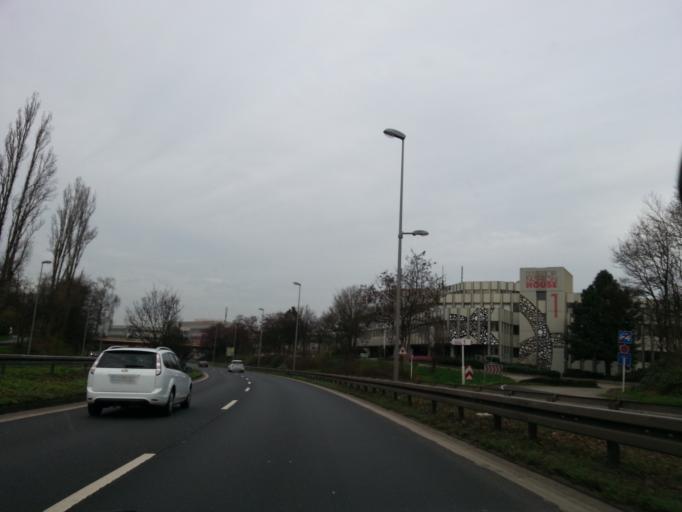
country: DE
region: North Rhine-Westphalia
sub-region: Regierungsbezirk Dusseldorf
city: Dusseldorf
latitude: 51.2604
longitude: 6.7619
